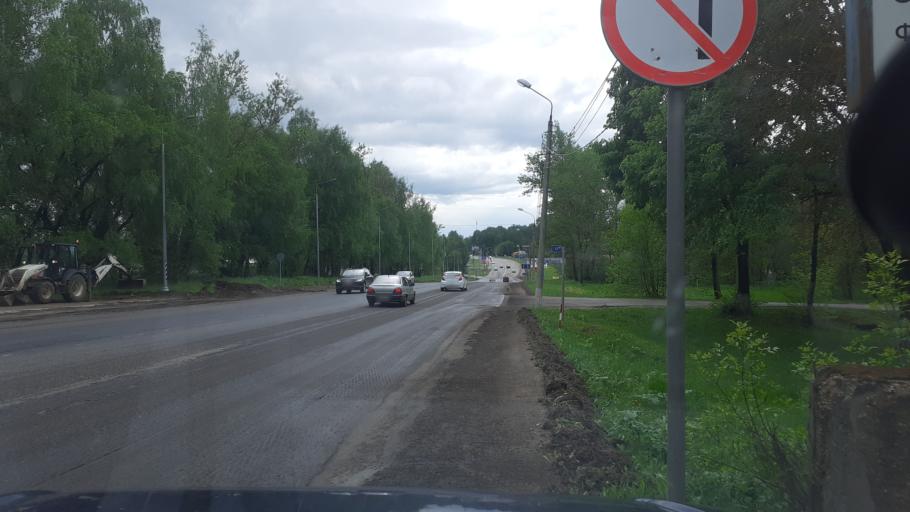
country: RU
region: Moskovskaya
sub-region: Volokolamskiy Rayon
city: Volokolamsk
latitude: 56.0231
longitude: 35.9435
